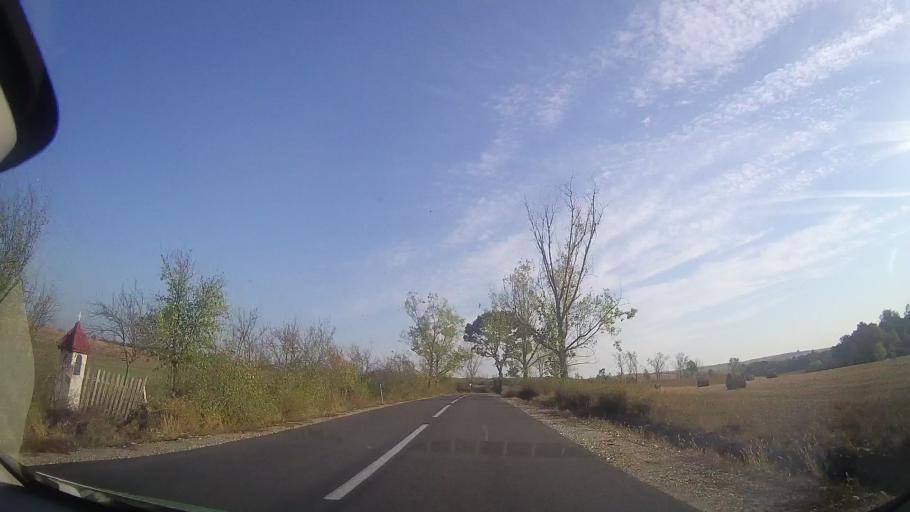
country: RO
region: Timis
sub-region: Comuna Masloc
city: Masloc
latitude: 45.9764
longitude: 21.4978
